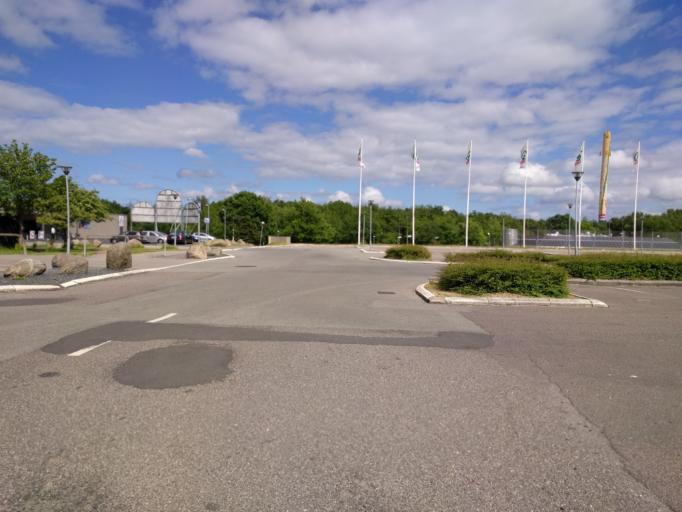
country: DK
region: South Denmark
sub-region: Odense Kommune
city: Seden
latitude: 55.4064
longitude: 10.4408
